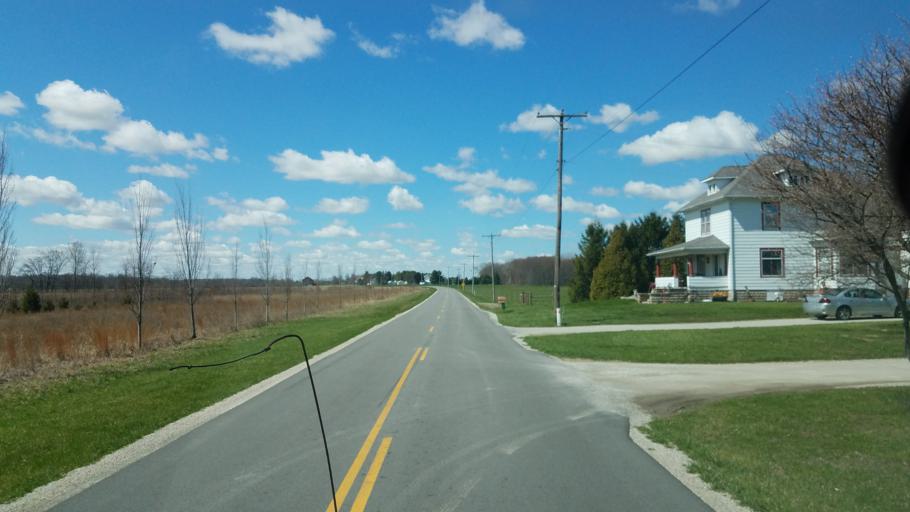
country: US
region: Ohio
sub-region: Seneca County
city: Fostoria
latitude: 41.1580
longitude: -83.4743
